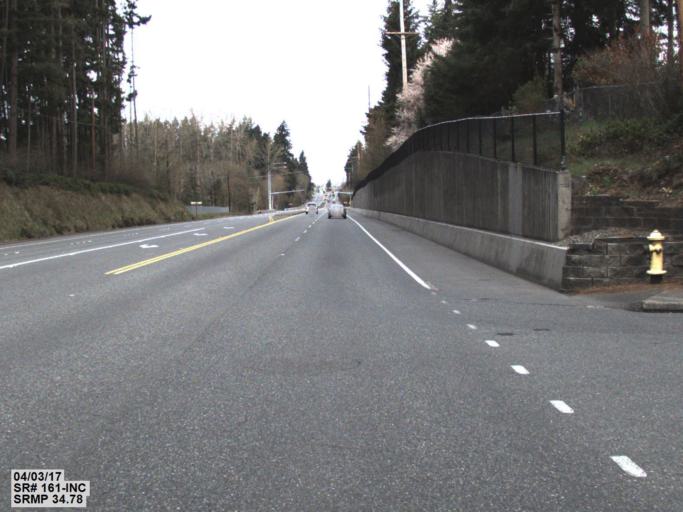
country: US
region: Washington
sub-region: Pierce County
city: Edgewood
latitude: 47.2697
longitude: -122.3037
